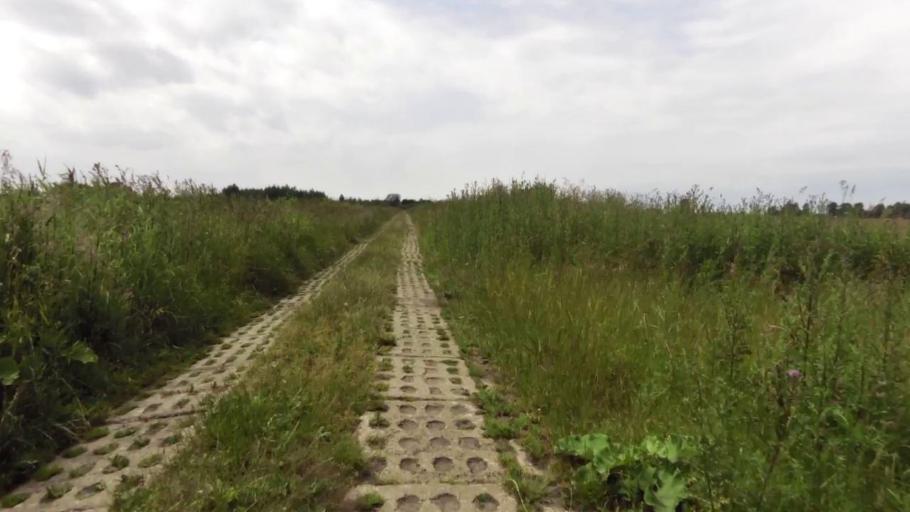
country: PL
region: West Pomeranian Voivodeship
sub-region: Powiat goleniowski
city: Stepnica
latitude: 53.7144
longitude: 14.5865
